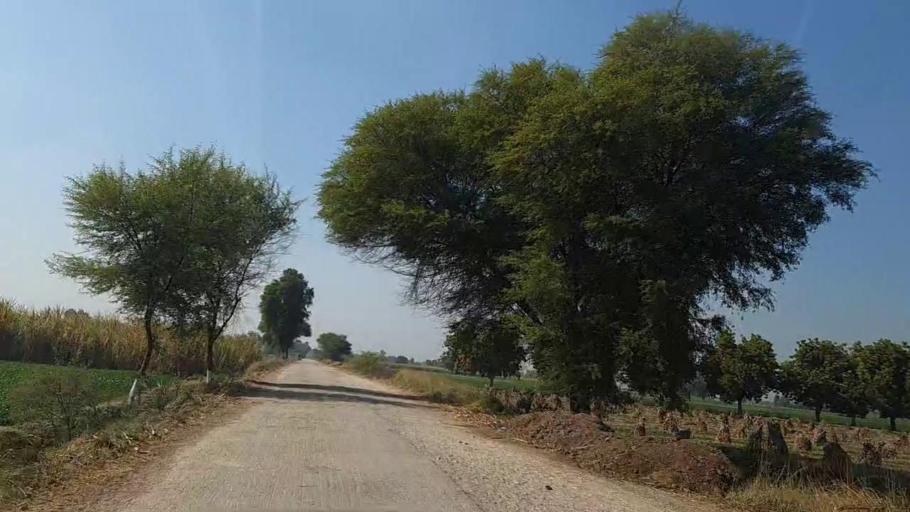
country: PK
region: Sindh
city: Sakrand
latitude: 26.2906
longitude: 68.1001
